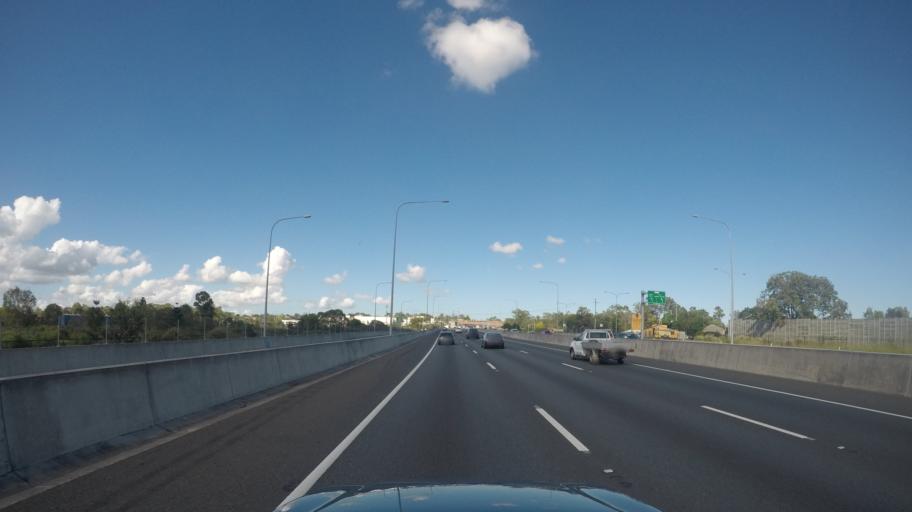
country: AU
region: Queensland
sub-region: Ipswich
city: Redbank
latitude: -27.6032
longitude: 152.8723
